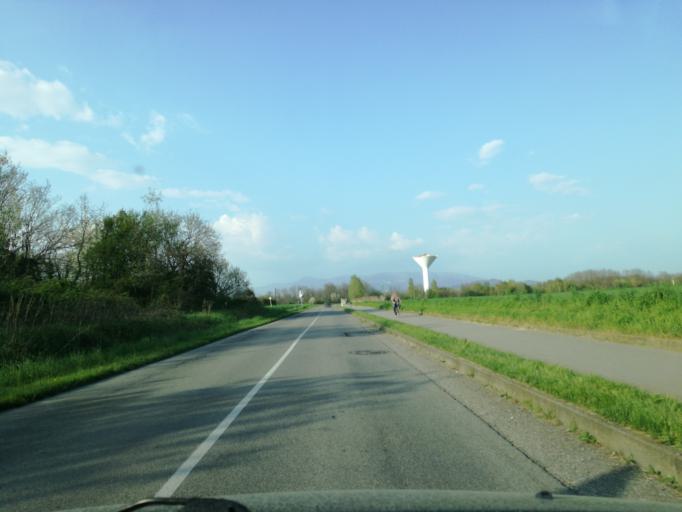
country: IT
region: Lombardy
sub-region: Provincia di Monza e Brianza
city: Carnate
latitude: 45.6543
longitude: 9.3836
